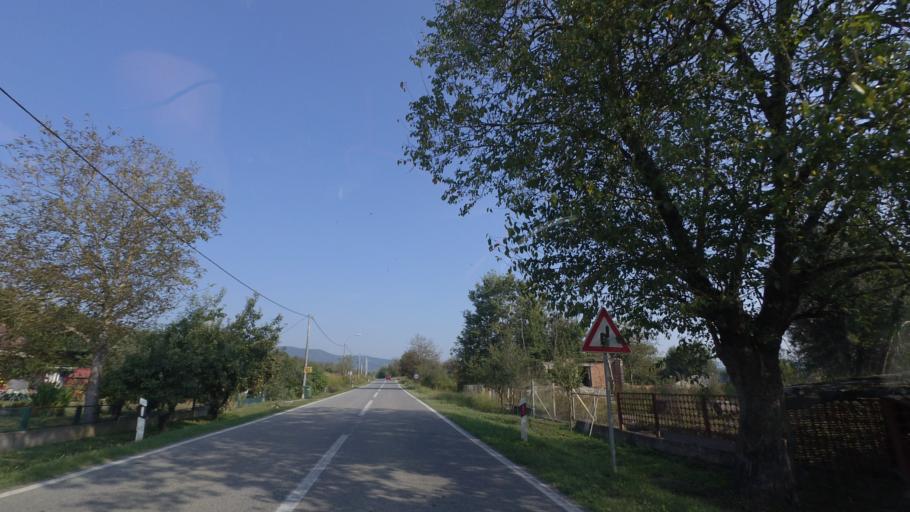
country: HR
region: Brodsko-Posavska
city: Resetari
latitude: 45.3856
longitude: 17.5103
